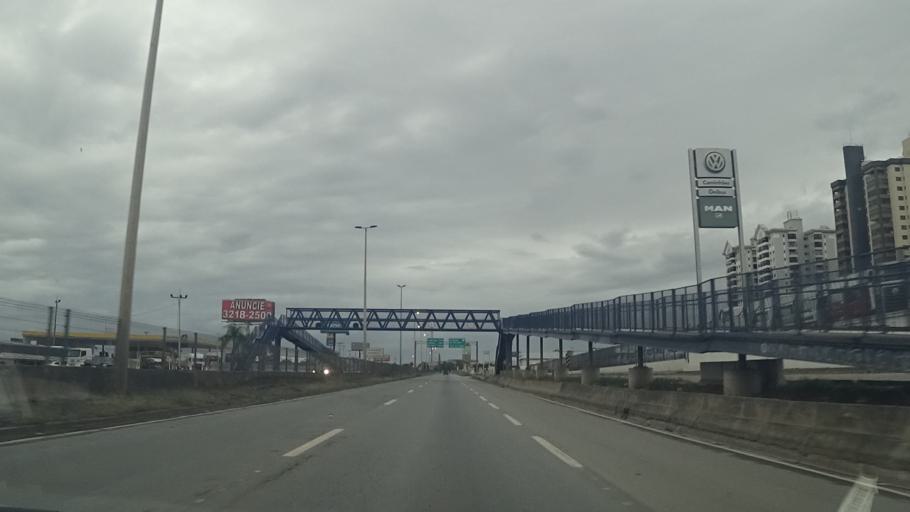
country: BR
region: Goias
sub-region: Goiania
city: Goiania
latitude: -16.7147
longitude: -49.2349
